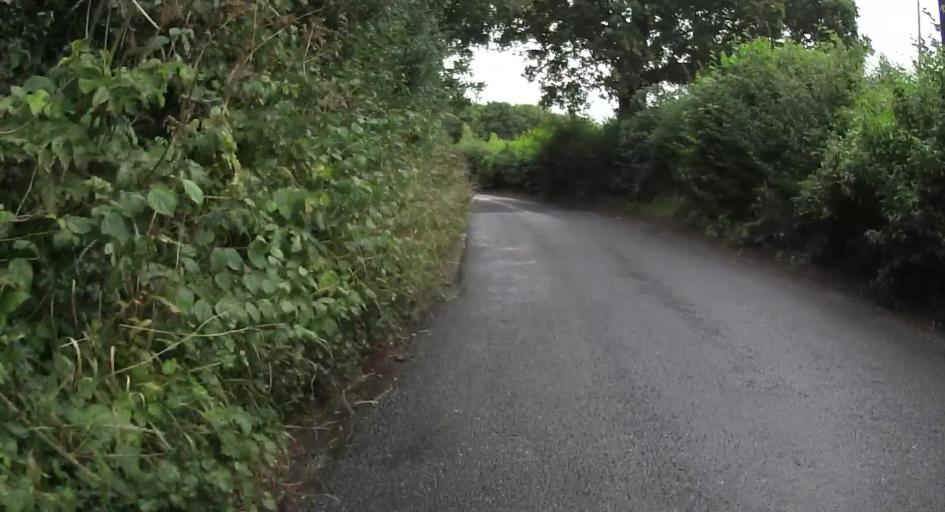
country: GB
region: England
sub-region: Hampshire
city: Andover
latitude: 51.2446
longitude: -1.4118
